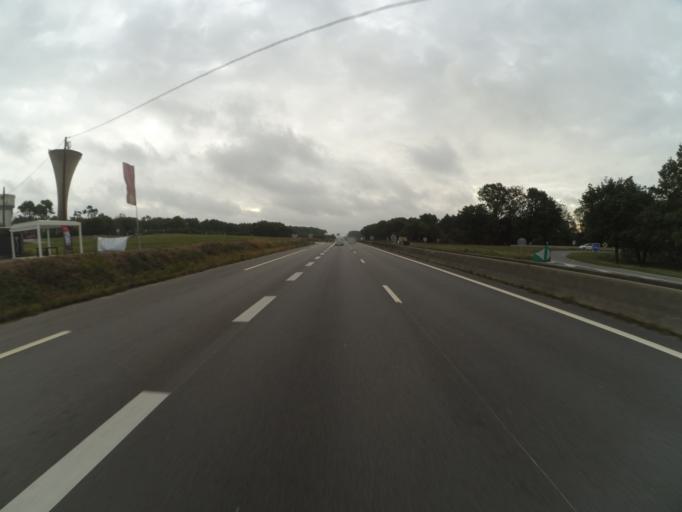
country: FR
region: Brittany
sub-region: Departement du Morbihan
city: Plougoumelen
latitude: 47.6649
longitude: -2.8983
